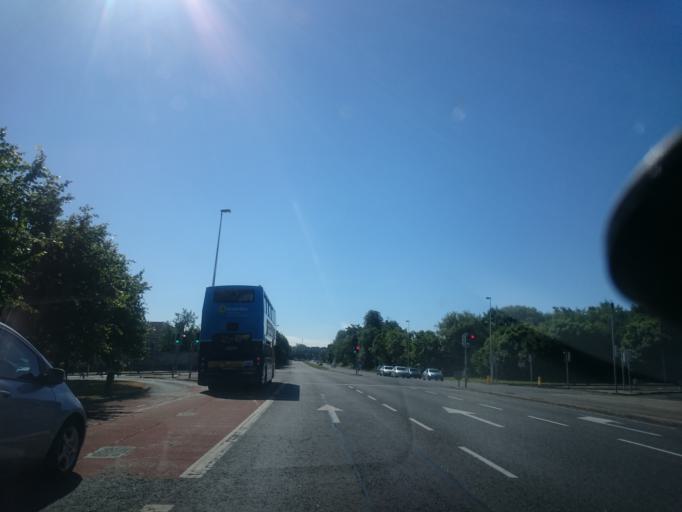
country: IE
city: Booterstown
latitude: 53.2934
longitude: -6.2016
